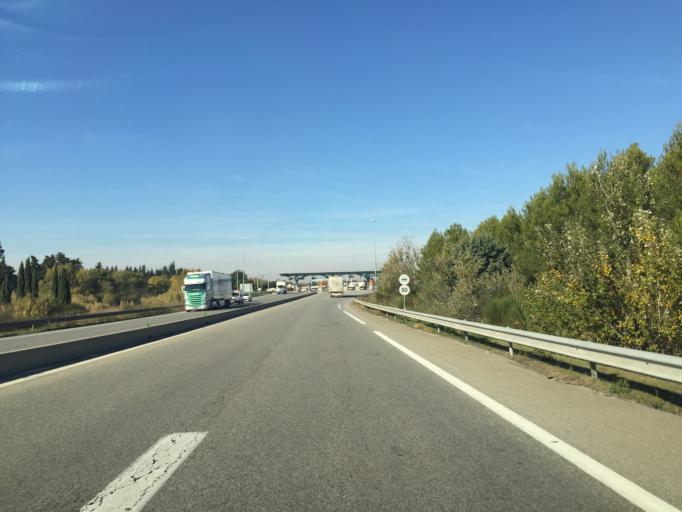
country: FR
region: Provence-Alpes-Cote d'Azur
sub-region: Departement du Vaucluse
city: Cavaillon
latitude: 43.8182
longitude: 5.0294
